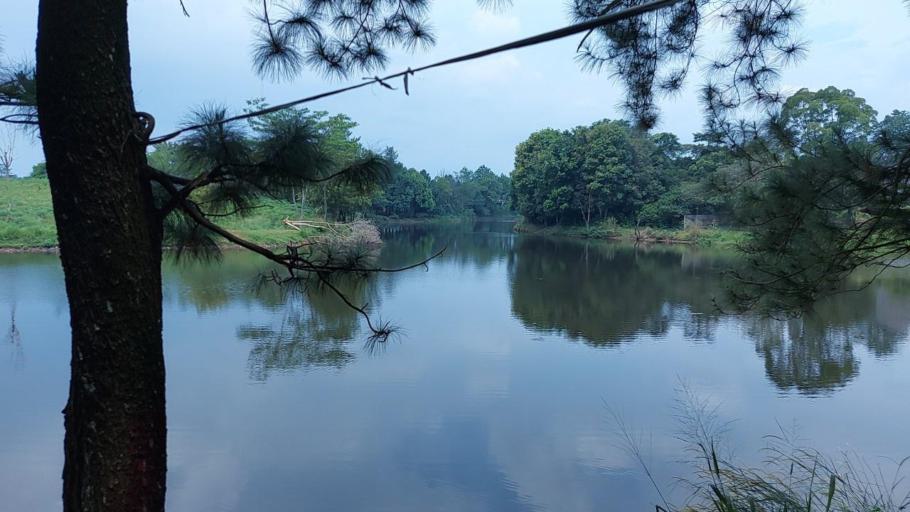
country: ID
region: West Java
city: Cibinong
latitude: -6.5092
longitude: 106.7786
